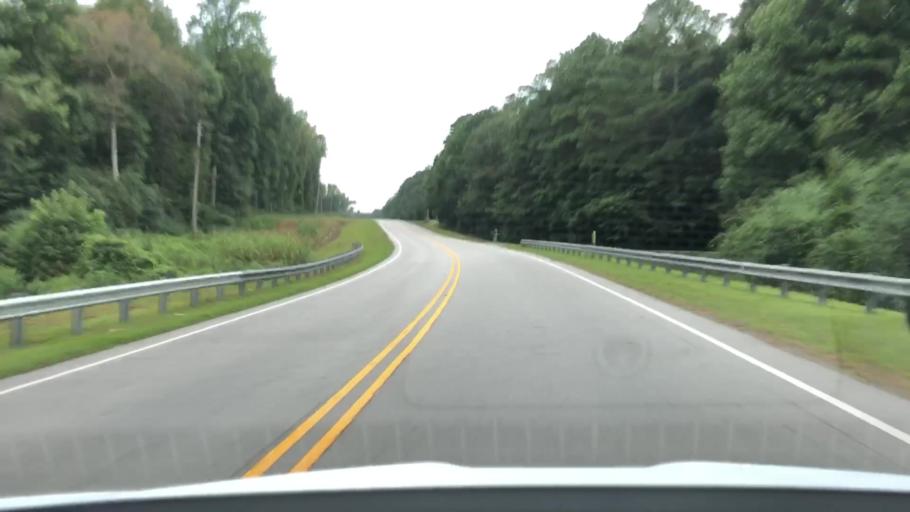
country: US
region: North Carolina
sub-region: Jones County
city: Trenton
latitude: 35.0329
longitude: -77.3184
